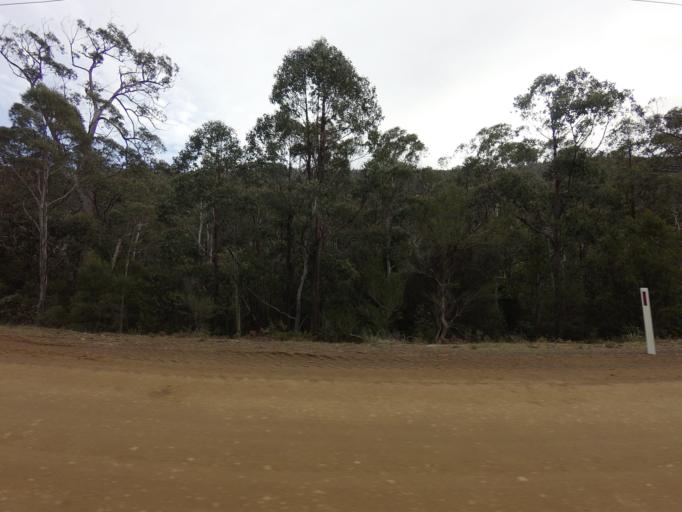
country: AU
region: Tasmania
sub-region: Huon Valley
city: Huonville
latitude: -43.0589
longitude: 147.0955
